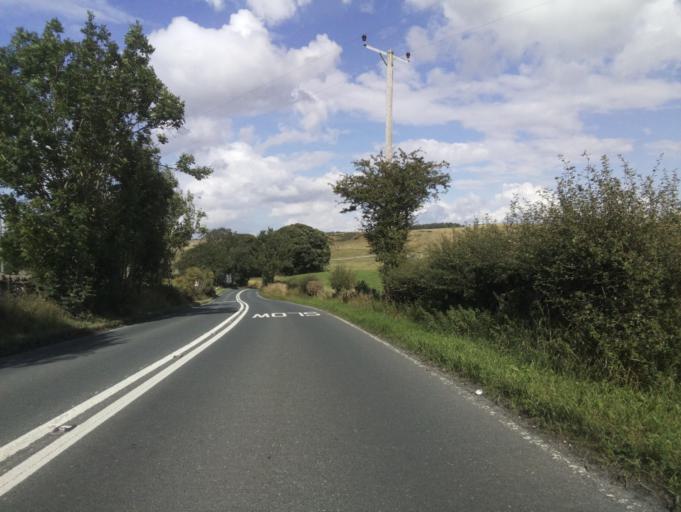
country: GB
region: England
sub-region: North Yorkshire
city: Leyburn
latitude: 54.3485
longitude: -1.8094
